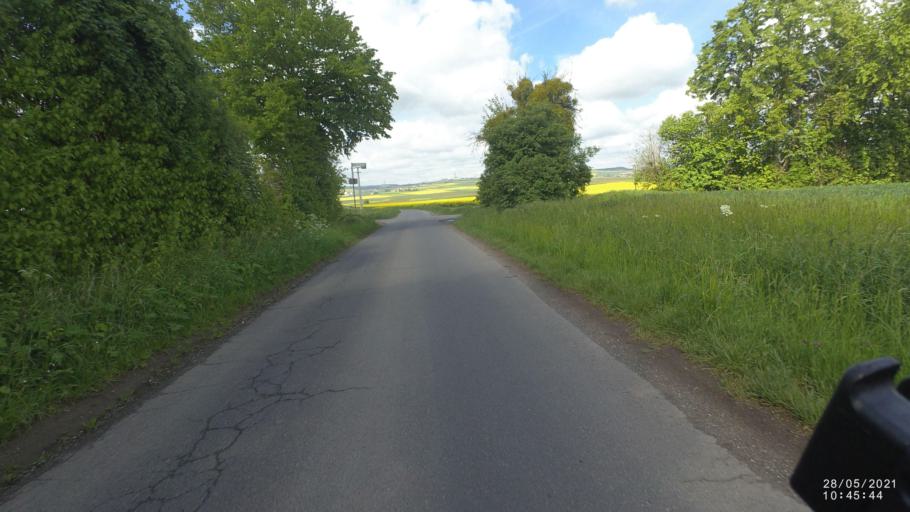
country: DE
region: Rheinland-Pfalz
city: Munstermaifeld
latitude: 50.2455
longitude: 7.3497
